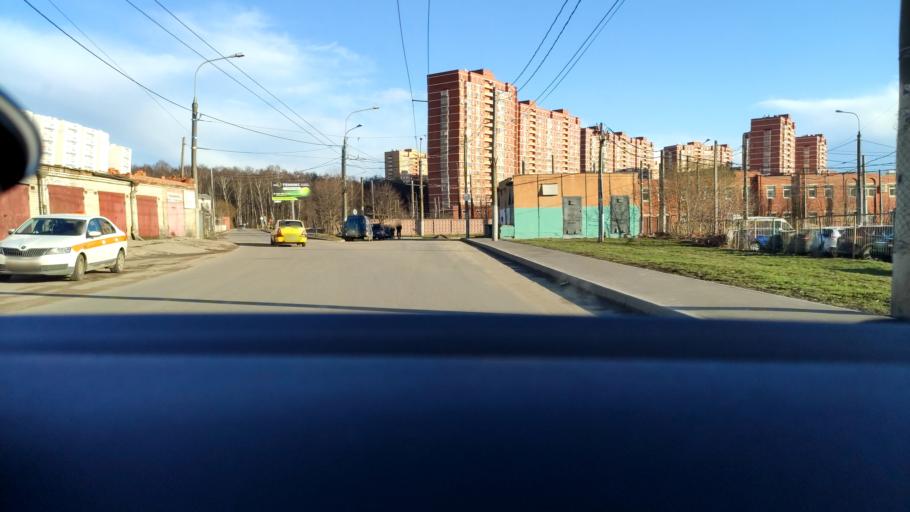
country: RU
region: Moskovskaya
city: Vidnoye
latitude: 55.5491
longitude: 37.7193
